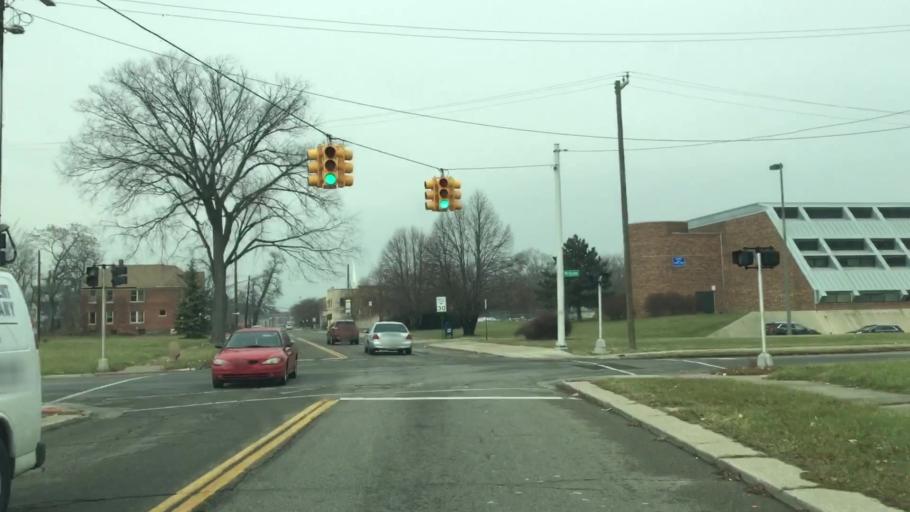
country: US
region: Michigan
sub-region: Wayne County
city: Highland Park
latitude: 42.3559
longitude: -83.0961
